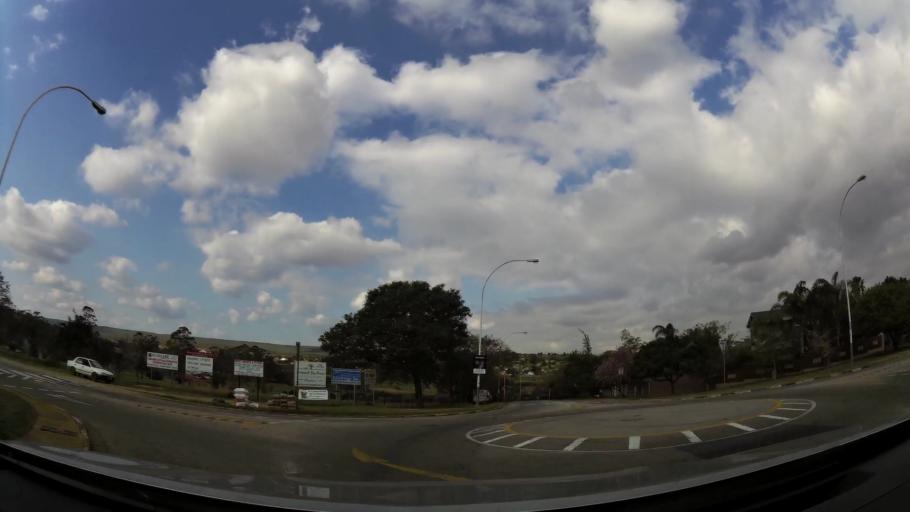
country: ZA
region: Eastern Cape
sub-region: Nelson Mandela Bay Metropolitan Municipality
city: Uitenhage
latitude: -33.7452
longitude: 25.4109
